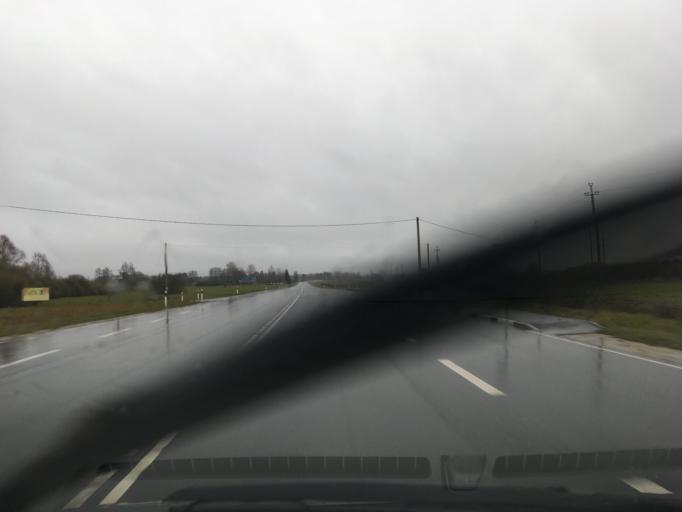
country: EE
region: Harju
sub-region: Nissi vald
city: Turba
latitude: 58.8840
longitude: 24.0894
